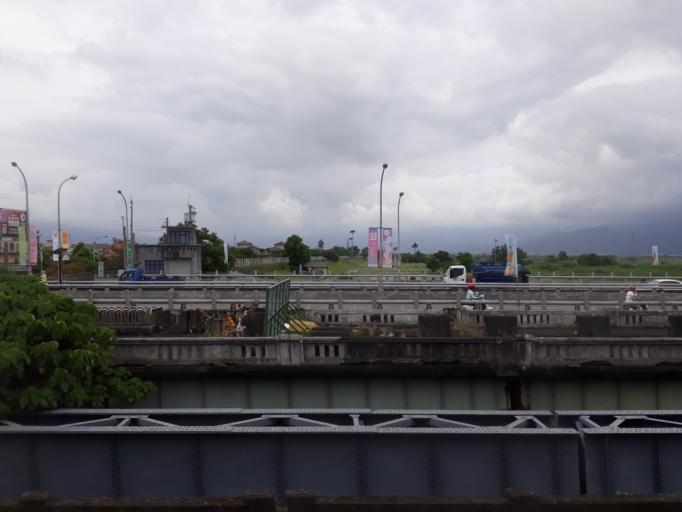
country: TW
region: Taiwan
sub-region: Yilan
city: Yilan
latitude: 24.7120
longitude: 121.7730
